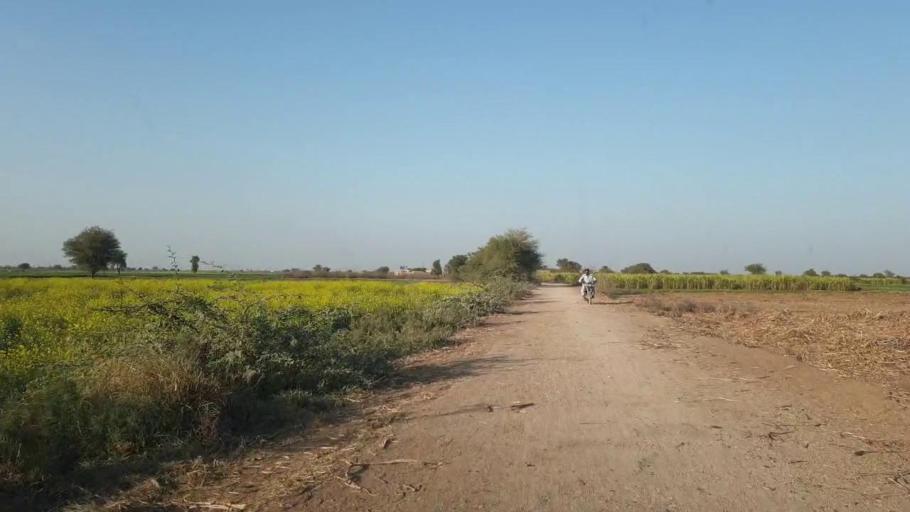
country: PK
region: Sindh
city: Tando Allahyar
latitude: 25.3739
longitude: 68.7082
